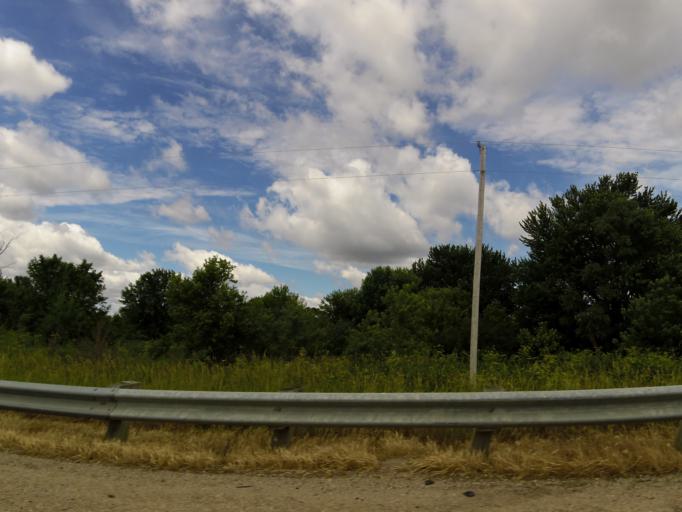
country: US
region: Iowa
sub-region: Chickasaw County
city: New Hampton
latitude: 43.2094
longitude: -92.2984
